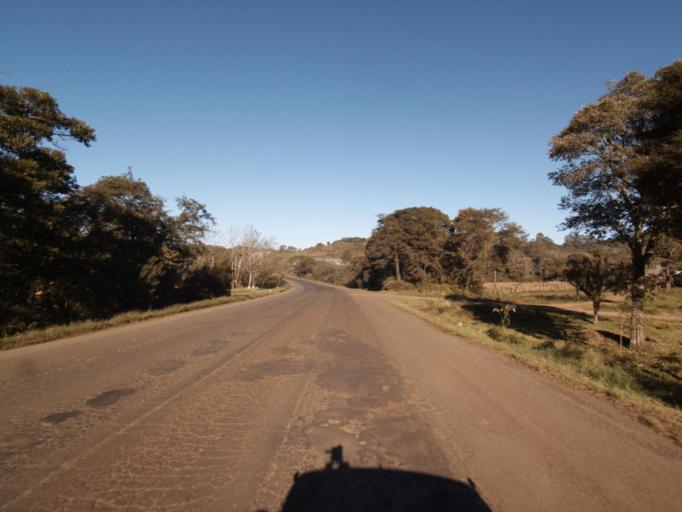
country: BR
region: Rio Grande do Sul
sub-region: Frederico Westphalen
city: Frederico Westphalen
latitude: -26.8935
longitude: -53.1884
